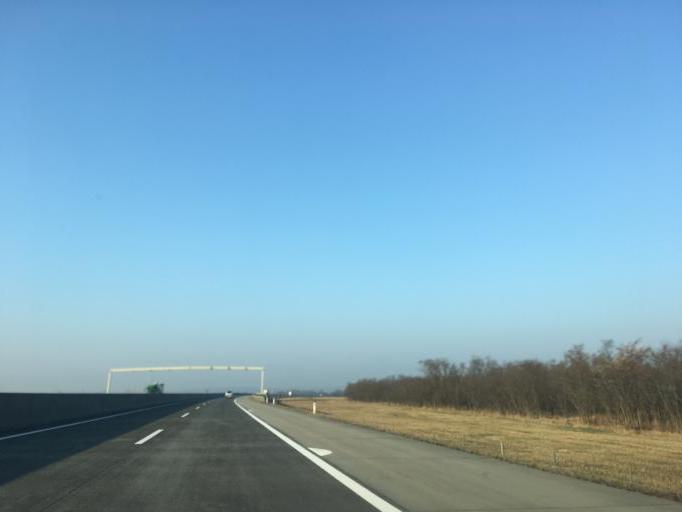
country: AT
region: Burgenland
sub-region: Politischer Bezirk Neusiedl am See
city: Parndorf
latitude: 48.0346
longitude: 16.8879
